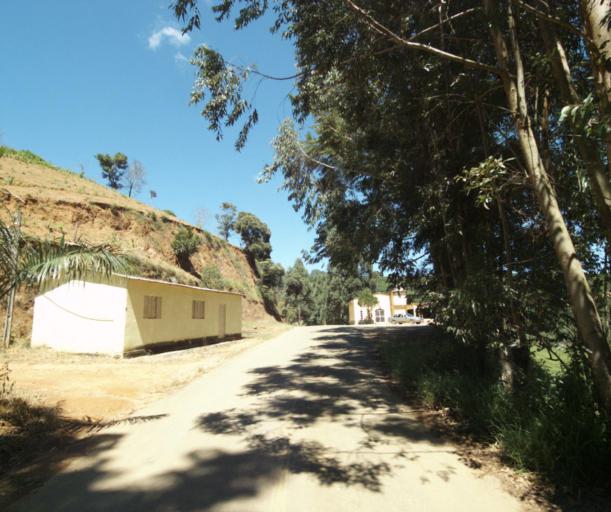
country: BR
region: Minas Gerais
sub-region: Espera Feliz
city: Espera Feliz
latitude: -20.6036
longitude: -41.8329
